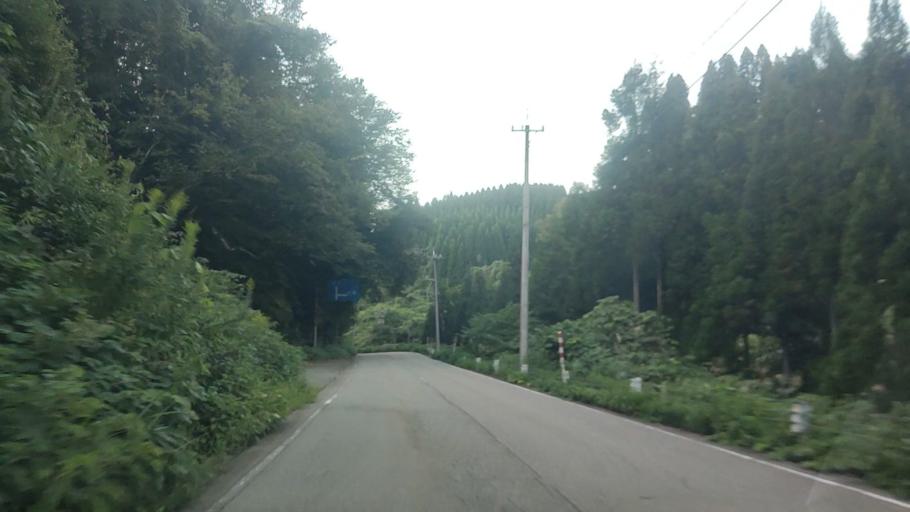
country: JP
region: Ishikawa
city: Tsubata
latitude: 36.6344
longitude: 136.7703
